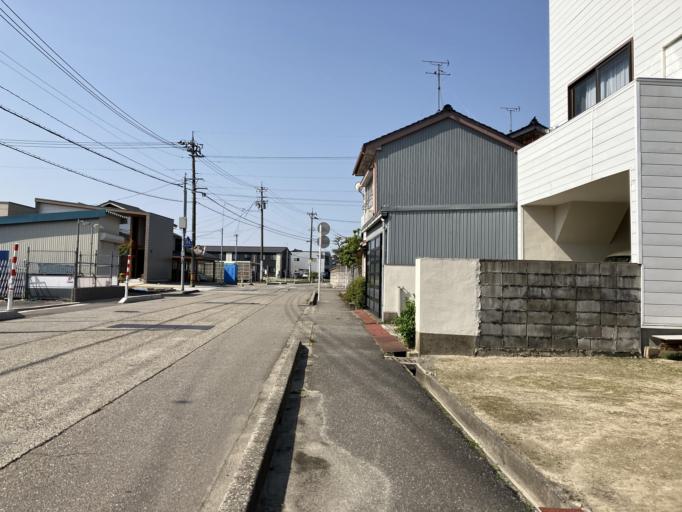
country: JP
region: Toyama
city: Takaoka
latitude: 36.7467
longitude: 137.0259
